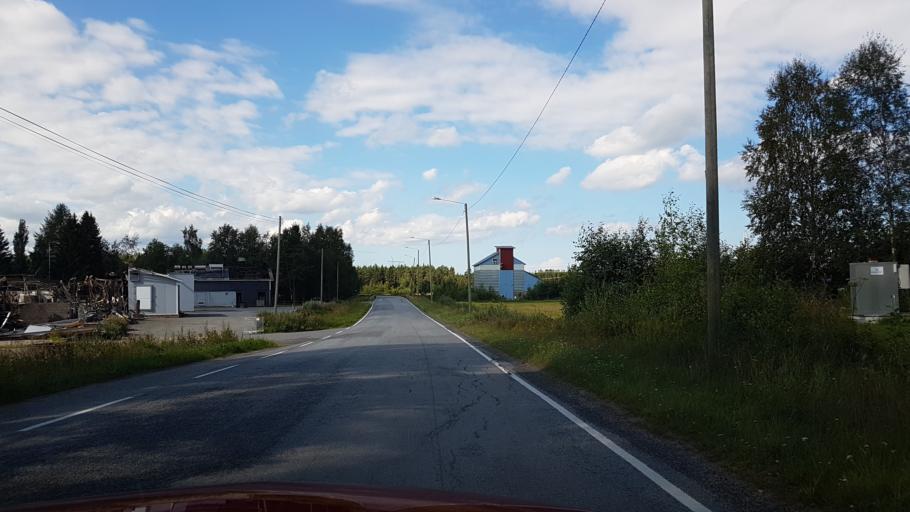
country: FI
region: Northern Ostrobothnia
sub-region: Ylivieska
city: Himanka
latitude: 64.0939
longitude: 23.7724
